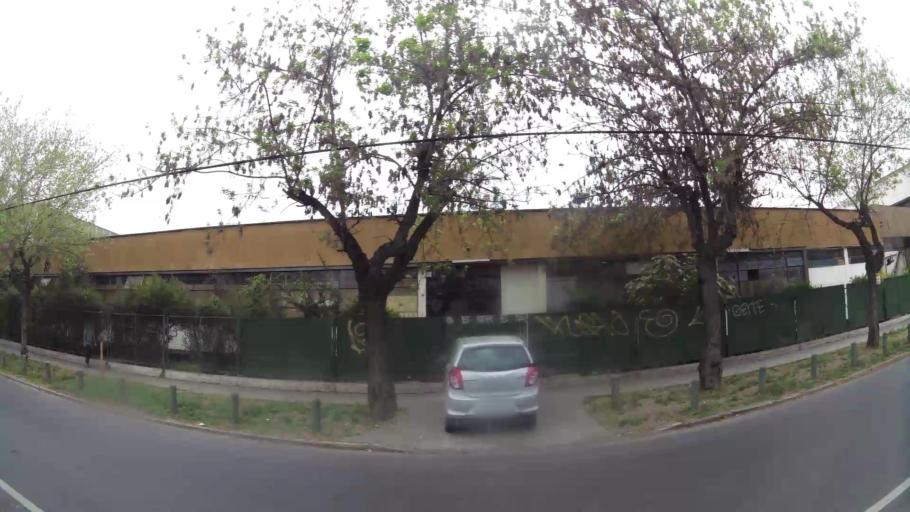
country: CL
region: Santiago Metropolitan
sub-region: Provincia de Santiago
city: Villa Presidente Frei, Nunoa, Santiago, Chile
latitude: -33.4827
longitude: -70.6061
